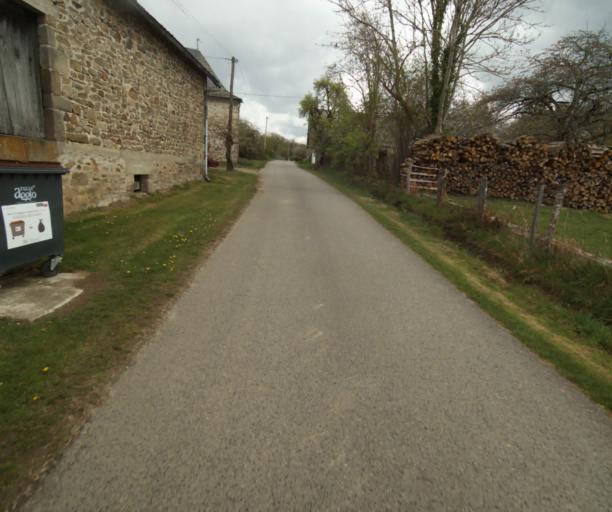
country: FR
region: Limousin
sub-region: Departement de la Correze
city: Laguenne
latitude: 45.2526
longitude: 1.8744
